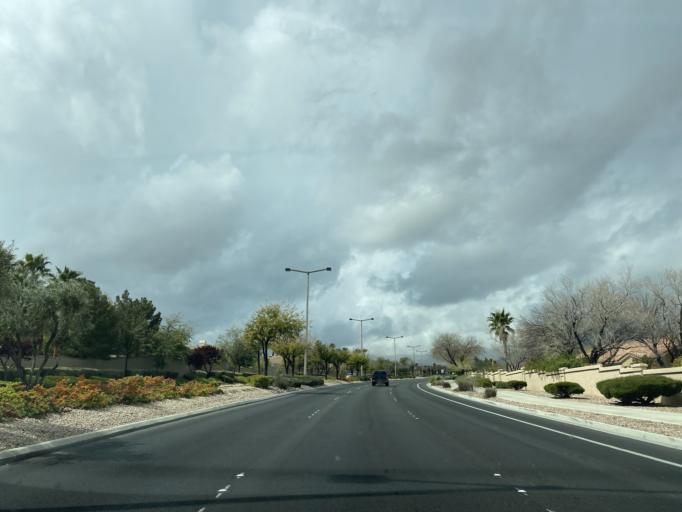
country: US
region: Nevada
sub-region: Clark County
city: Summerlin South
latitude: 36.2043
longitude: -115.3095
